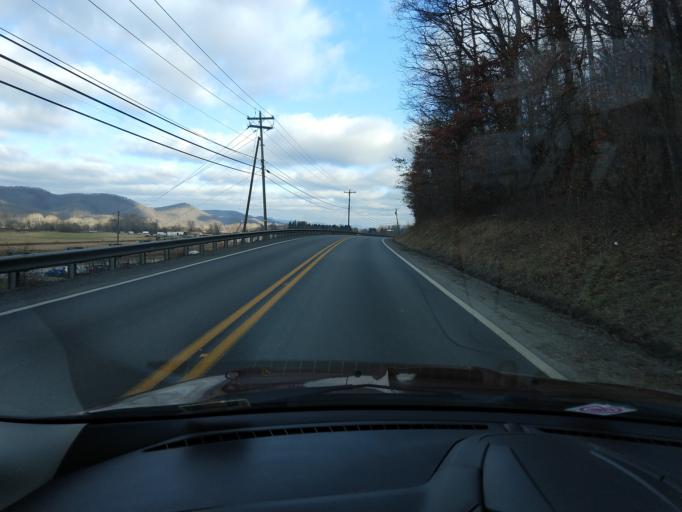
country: US
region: West Virginia
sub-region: Randolph County
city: Elkins
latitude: 38.8190
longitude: -79.8760
